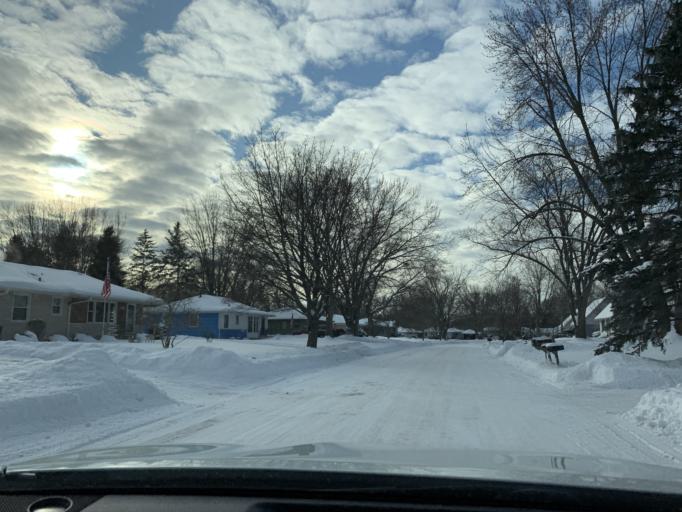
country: US
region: Minnesota
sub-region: Anoka County
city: Blaine
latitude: 45.1735
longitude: -93.2858
